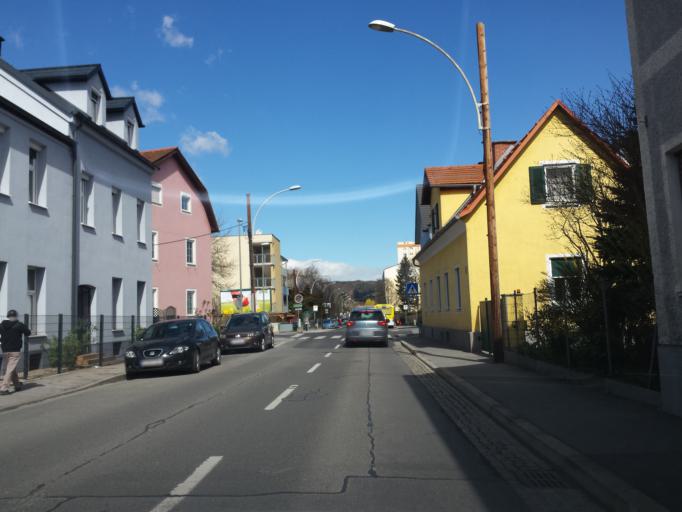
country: AT
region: Styria
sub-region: Graz Stadt
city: Goesting
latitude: 47.0927
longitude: 15.4139
